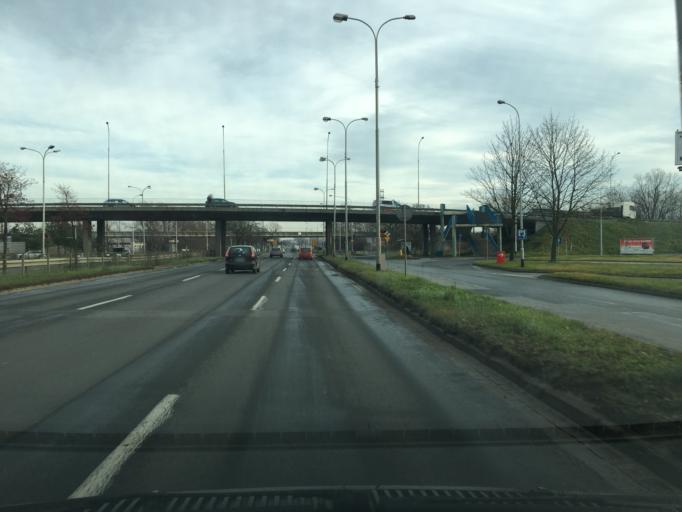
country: PL
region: Lower Silesian Voivodeship
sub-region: Powiat wroclawski
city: Wilczyce
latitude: 51.1414
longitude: 17.0921
